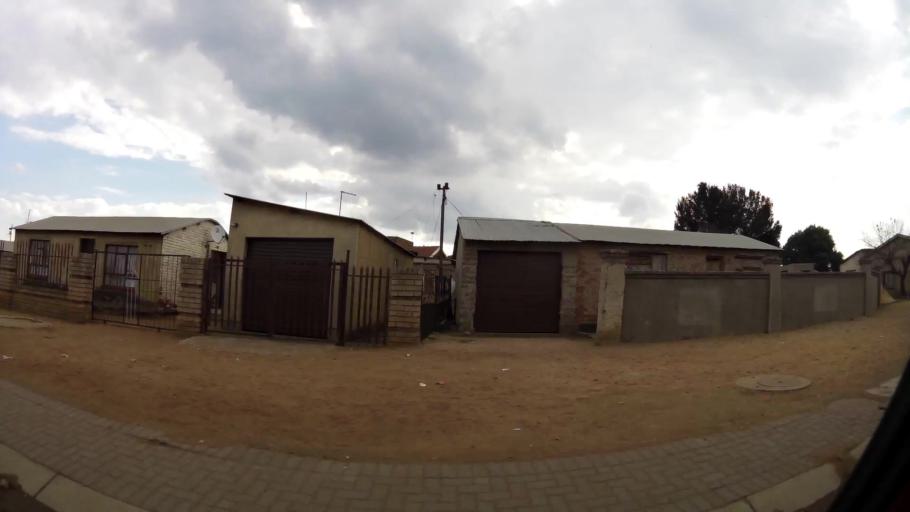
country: ZA
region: Gauteng
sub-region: Sedibeng District Municipality
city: Vanderbijlpark
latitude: -26.6638
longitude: 27.8511
